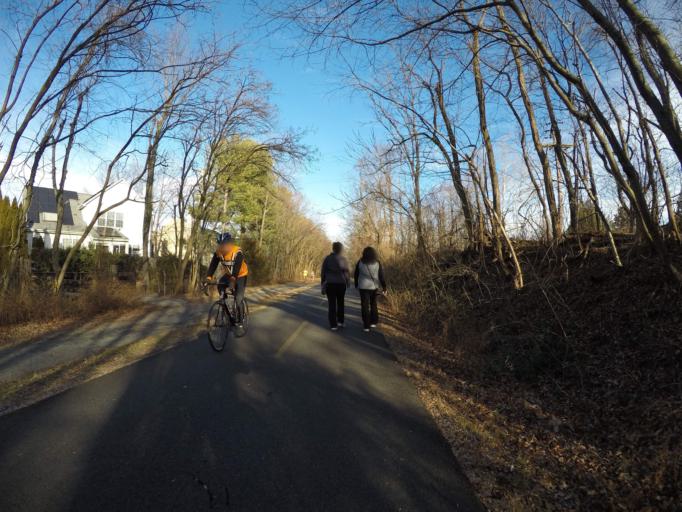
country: US
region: Virginia
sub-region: Loudoun County
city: Leesburg
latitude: 39.1114
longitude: -77.5830
